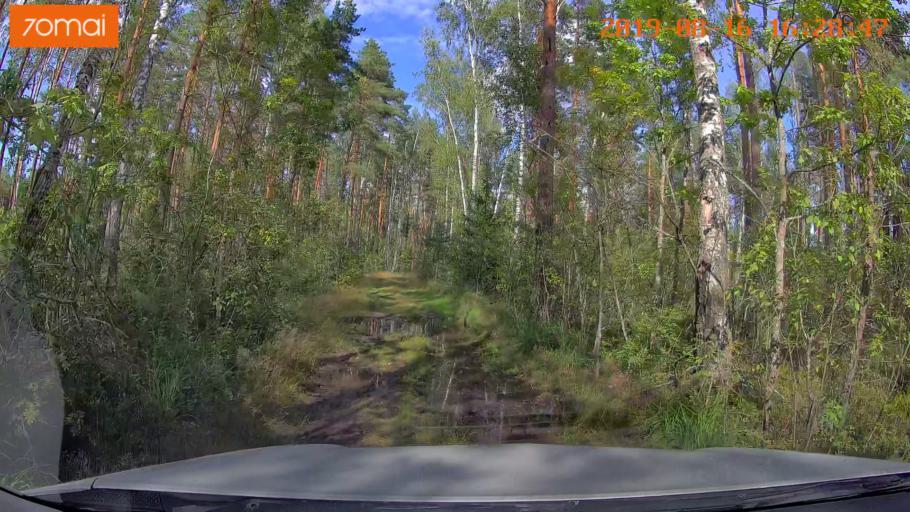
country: BY
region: Mogilev
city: Asipovichy
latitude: 53.2244
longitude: 28.7717
